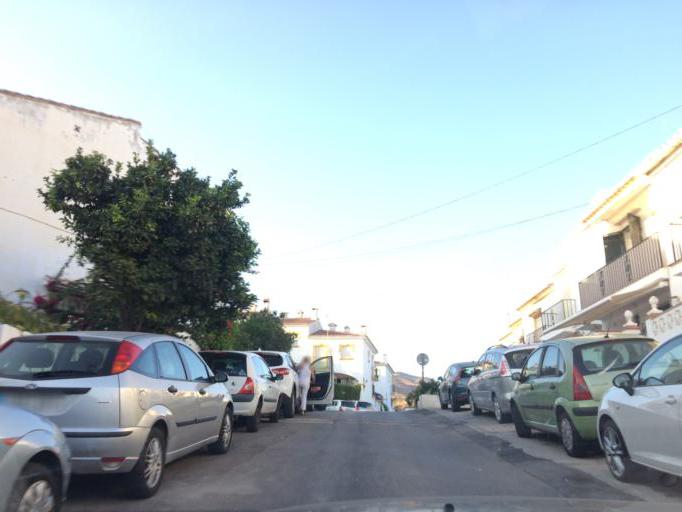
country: ES
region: Andalusia
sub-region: Provincia de Malaga
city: Rincon de la Victoria
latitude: 36.7204
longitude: -4.2966
